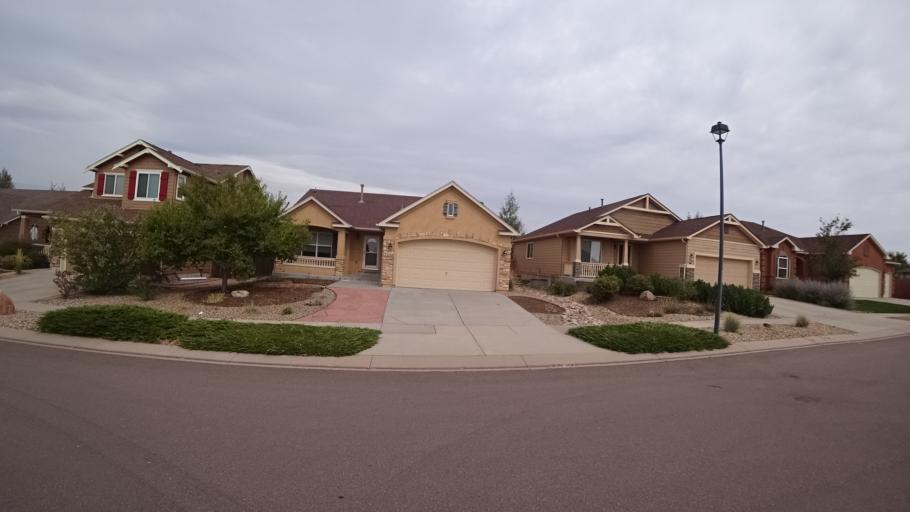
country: US
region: Colorado
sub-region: El Paso County
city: Cimarron Hills
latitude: 38.9206
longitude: -104.6865
